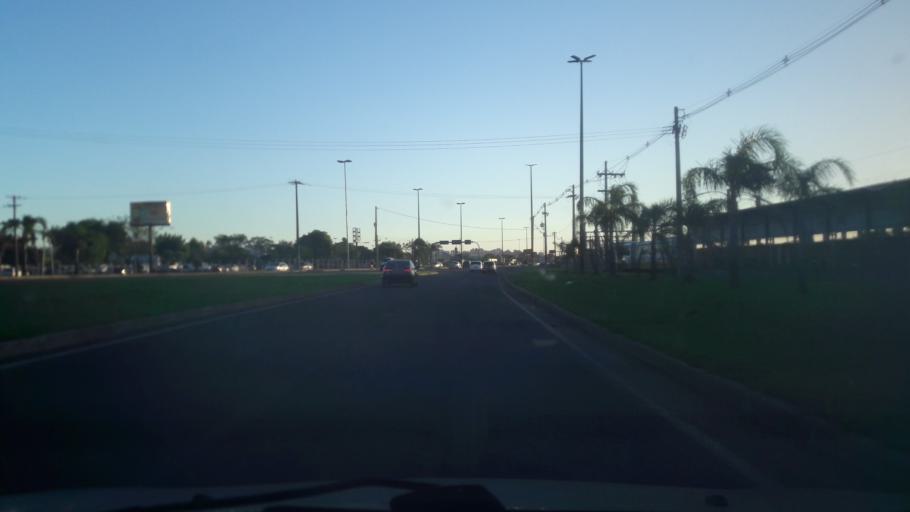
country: BR
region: Rio Grande do Sul
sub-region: Porto Alegre
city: Porto Alegre
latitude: -29.9885
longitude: -51.1828
